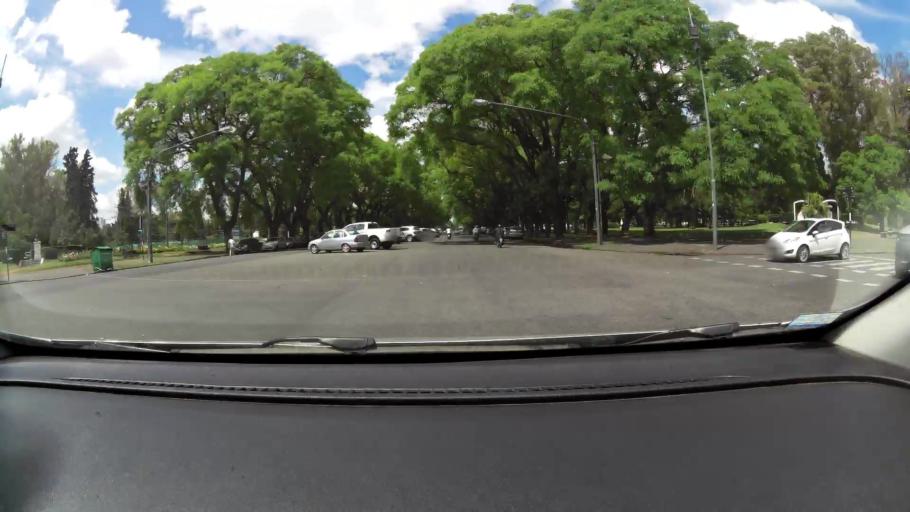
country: AR
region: Santa Fe
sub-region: Departamento de Rosario
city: Rosario
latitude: -32.9584
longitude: -60.6570
